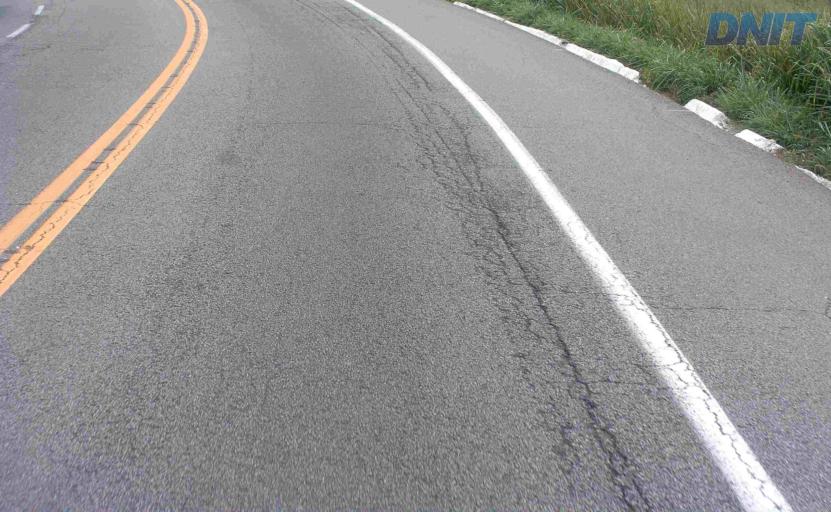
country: BR
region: Minas Gerais
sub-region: Caete
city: Caete
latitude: -19.7408
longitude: -43.6080
